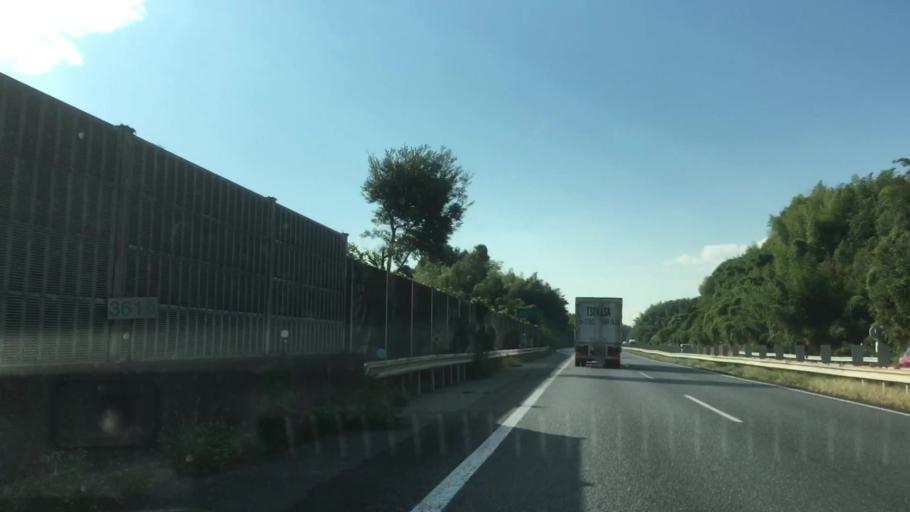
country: JP
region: Yamaguchi
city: Hikari
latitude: 34.0293
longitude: 131.9434
